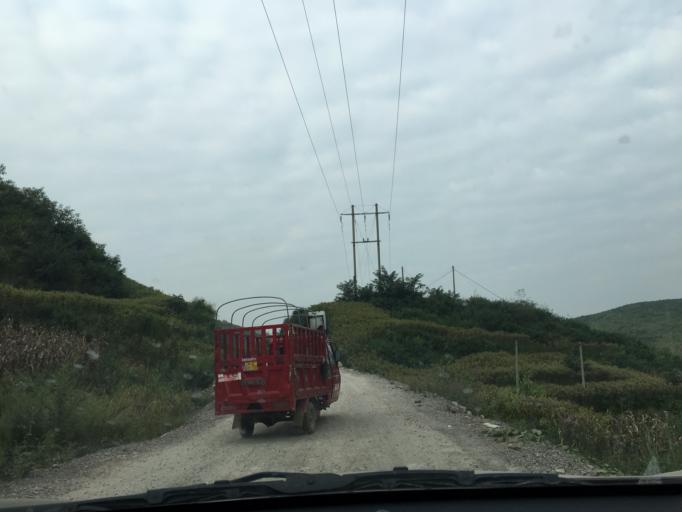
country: CN
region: Guangxi Zhuangzu Zizhiqu
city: Xinzhou
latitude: 25.4410
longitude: 105.4803
